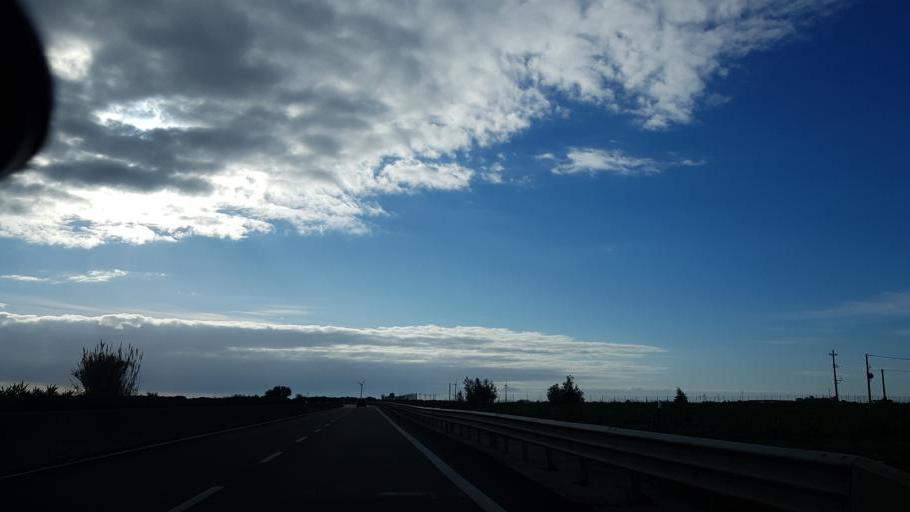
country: IT
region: Apulia
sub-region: Provincia di Brindisi
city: La Rosa
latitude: 40.5870
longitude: 17.9743
